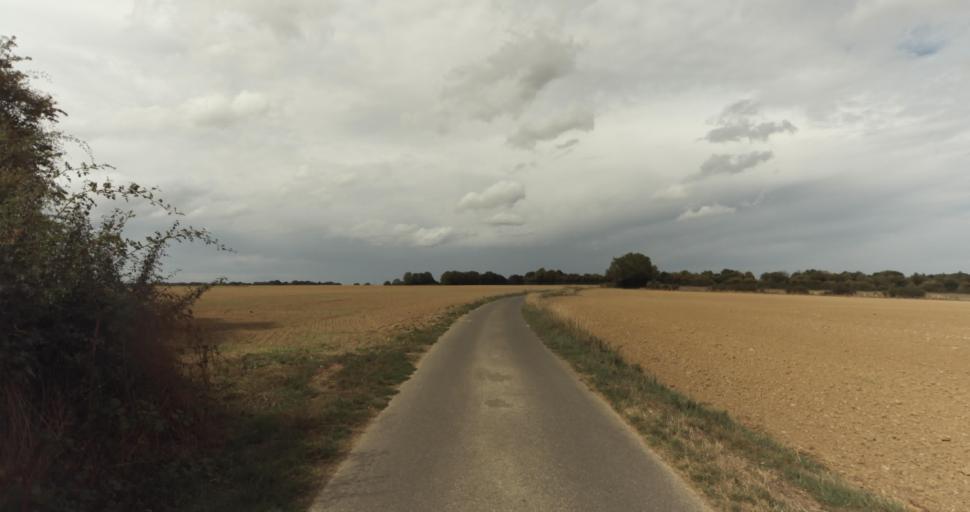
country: FR
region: Lower Normandy
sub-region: Departement du Calvados
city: Orbec
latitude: 48.9184
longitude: 0.3798
